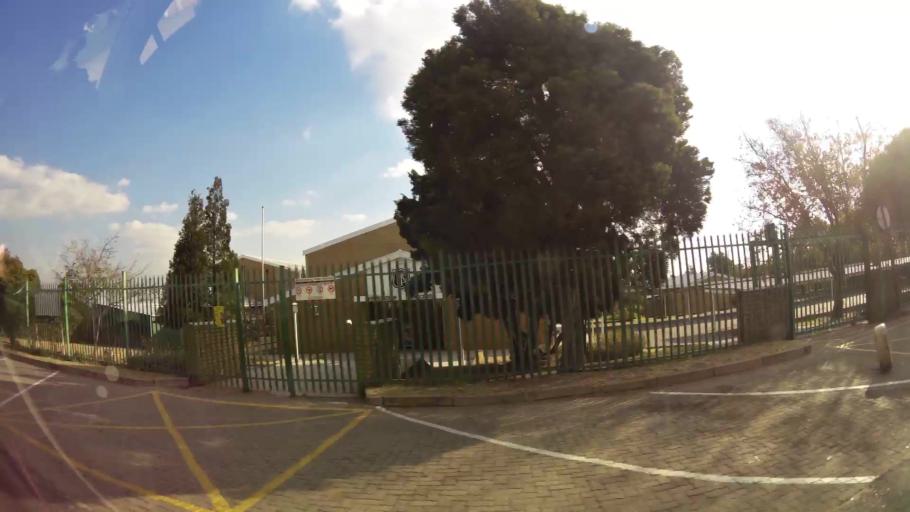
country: ZA
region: Gauteng
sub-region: West Rand District Municipality
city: Krugersdorp
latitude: -26.0909
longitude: 27.7626
